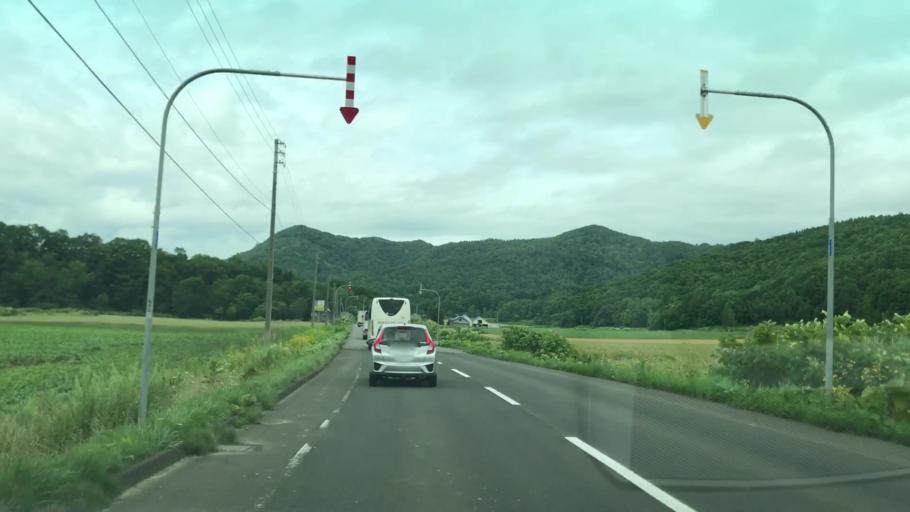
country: JP
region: Hokkaido
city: Niseko Town
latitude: 42.9469
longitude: 140.8374
